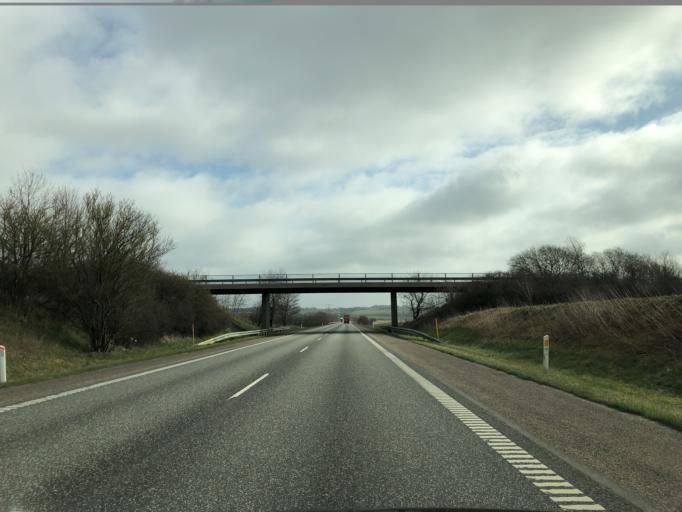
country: DK
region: North Denmark
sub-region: Rebild Kommune
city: Stovring
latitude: 56.8204
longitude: 9.6964
